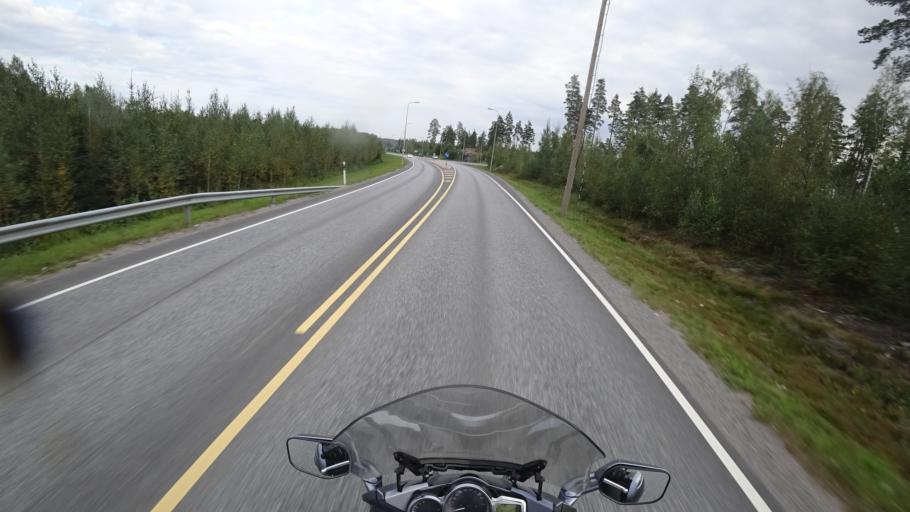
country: FI
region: Uusimaa
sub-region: Raaseporin
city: Karis
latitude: 60.0629
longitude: 23.6316
